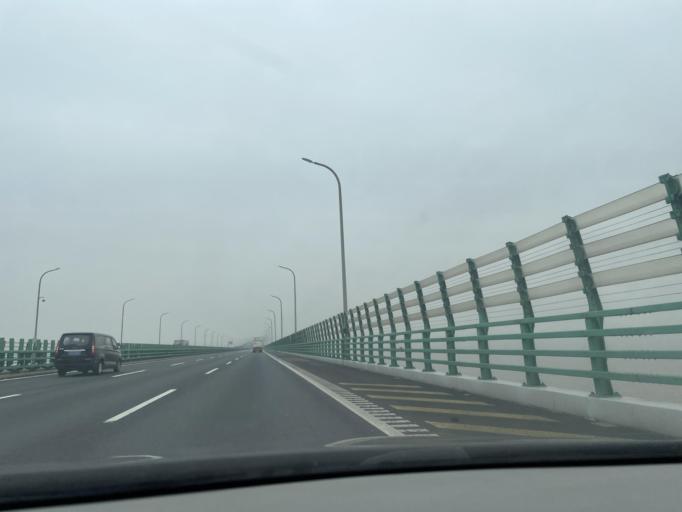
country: CN
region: Zhejiang Sheng
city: Zhapu
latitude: 30.4779
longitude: 121.1077
